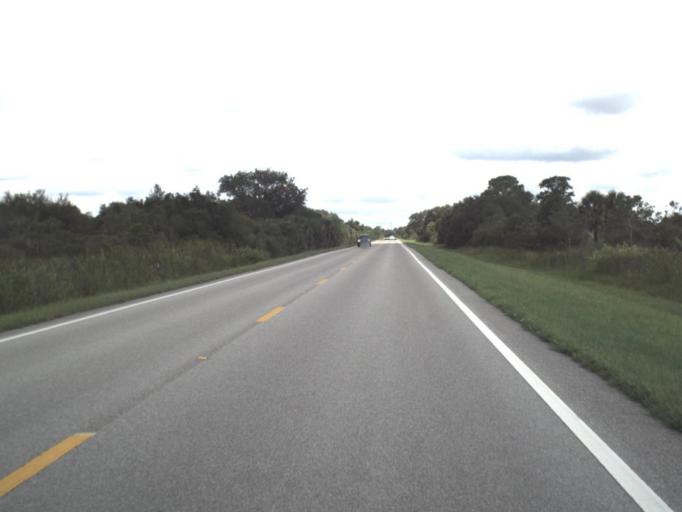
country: US
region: Florida
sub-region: Sarasota County
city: Warm Mineral Springs
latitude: 27.2098
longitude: -82.2557
